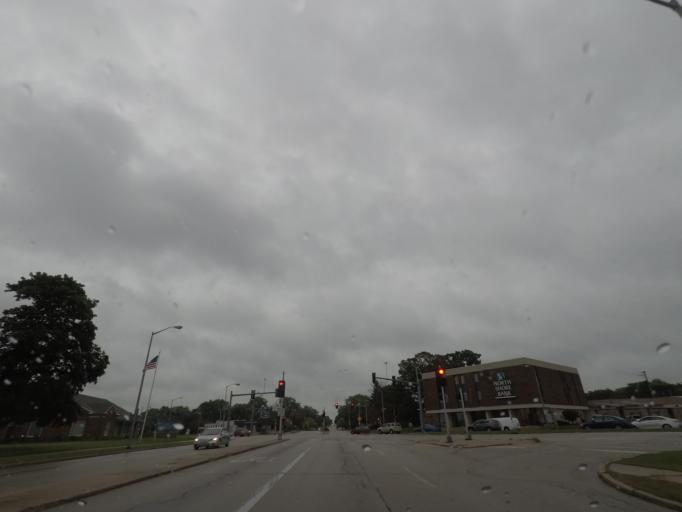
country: US
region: Wisconsin
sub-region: Milwaukee County
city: West Allis
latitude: 42.9953
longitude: -88.0451
